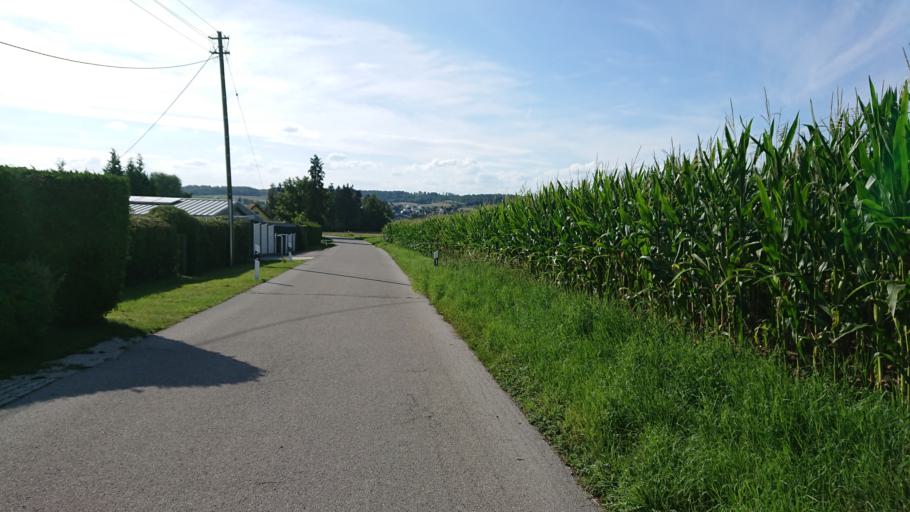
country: DE
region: Bavaria
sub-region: Swabia
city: Diedorf
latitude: 48.3711
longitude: 10.8058
